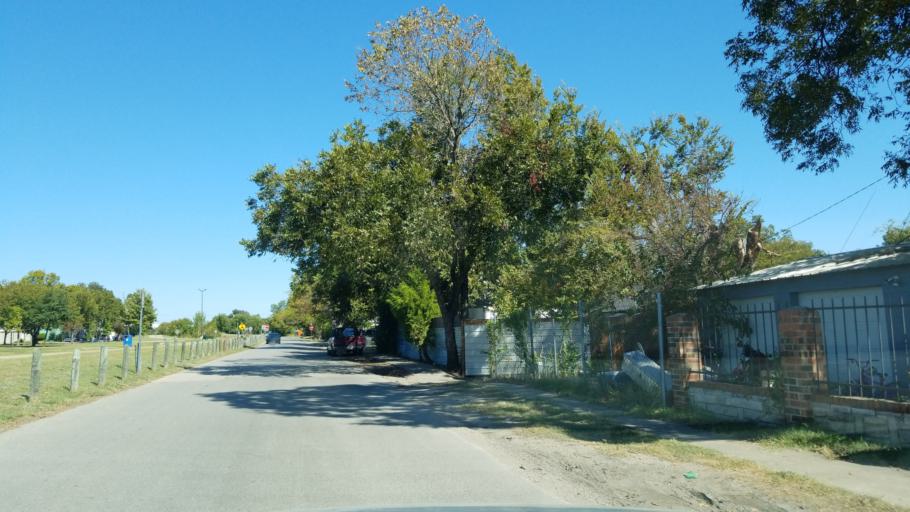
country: US
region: Texas
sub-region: Dallas County
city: Highland Park
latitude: 32.8023
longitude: -96.7505
